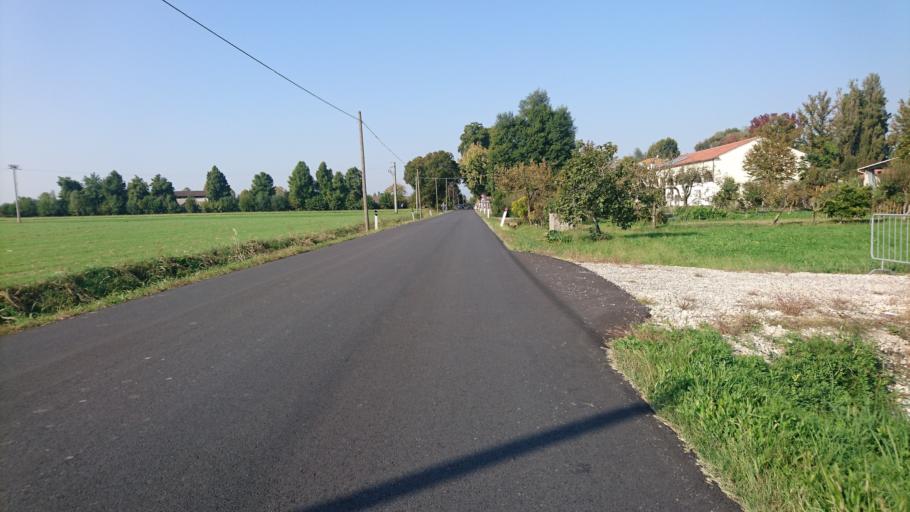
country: IT
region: Veneto
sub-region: Provincia di Padova
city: Gazzo
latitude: 45.5796
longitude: 11.6781
